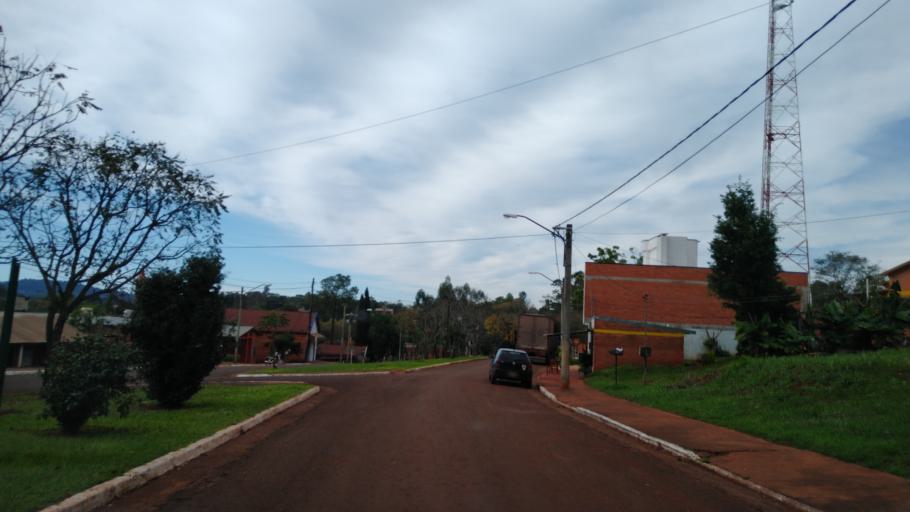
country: AR
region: Misiones
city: Capiovi
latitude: -26.9290
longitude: -55.0623
